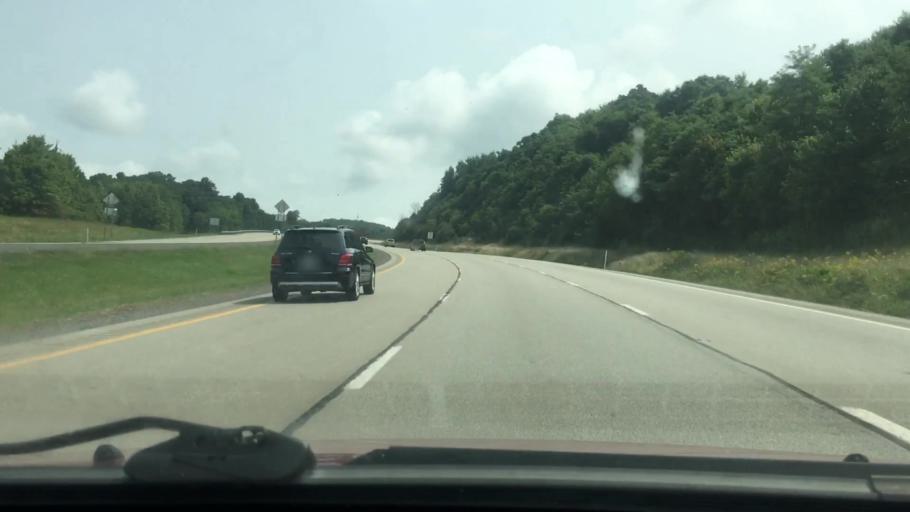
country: US
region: West Virginia
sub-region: Preston County
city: Terra Alta
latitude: 39.6576
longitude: -79.5104
